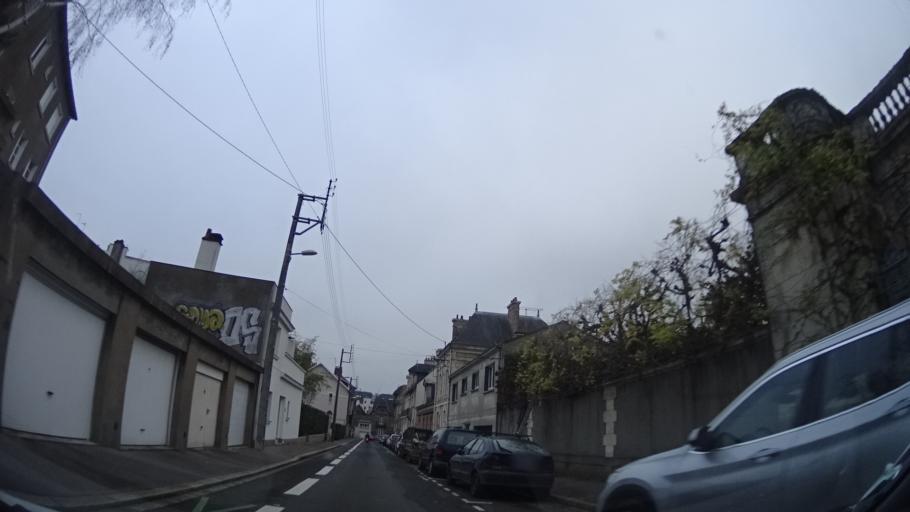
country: FR
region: Pays de la Loire
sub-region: Departement de la Loire-Atlantique
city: Nantes
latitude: 47.2205
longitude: -1.5707
